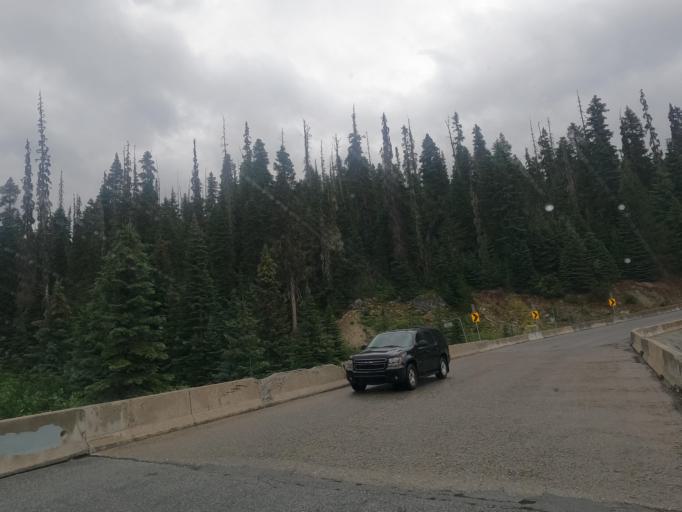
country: CA
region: British Columbia
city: Pemberton
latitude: 50.3847
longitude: -122.4696
